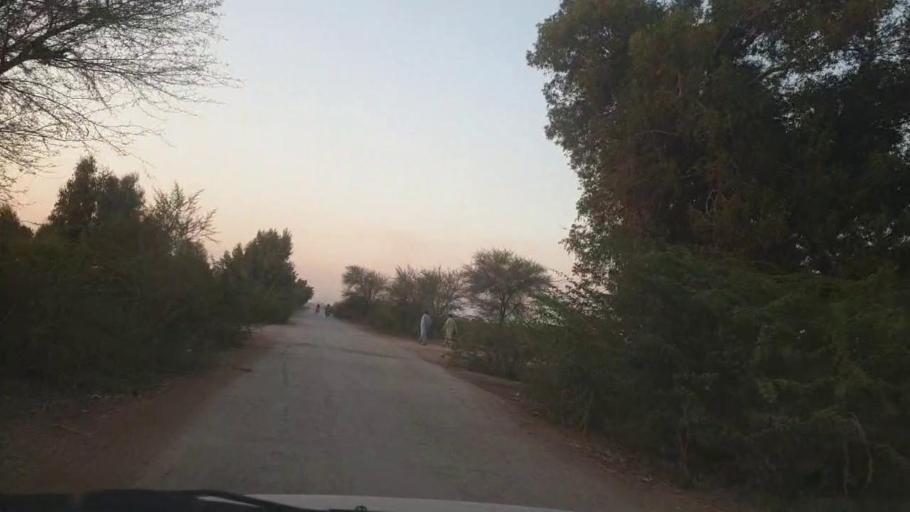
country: PK
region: Sindh
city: Mirpur Khas
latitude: 25.4848
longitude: 69.0435
